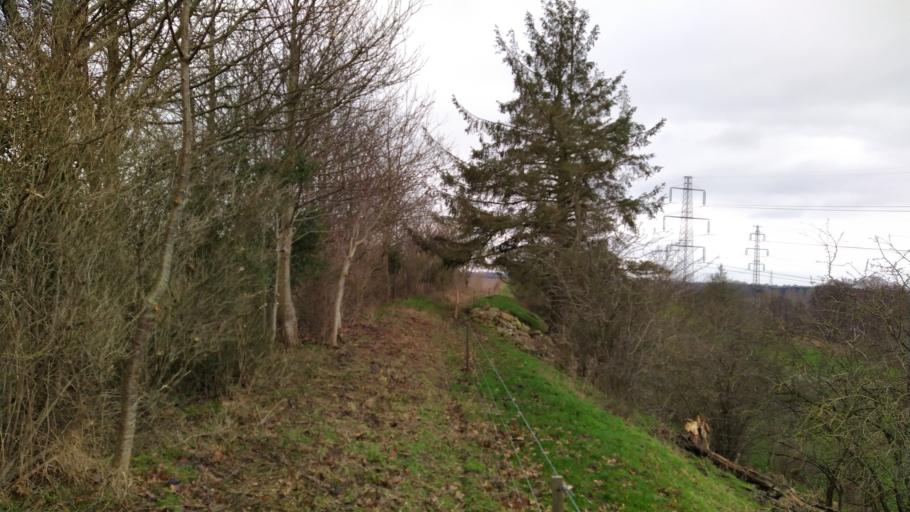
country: DK
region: Capital Region
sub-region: Egedal Kommune
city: Stenlose
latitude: 55.7558
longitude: 12.2153
